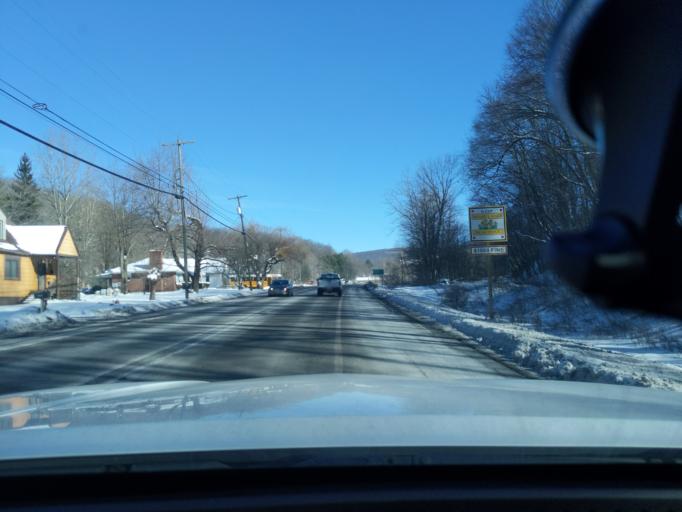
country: US
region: Maryland
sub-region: Allegany County
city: Lonaconing
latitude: 39.5792
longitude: -78.9699
